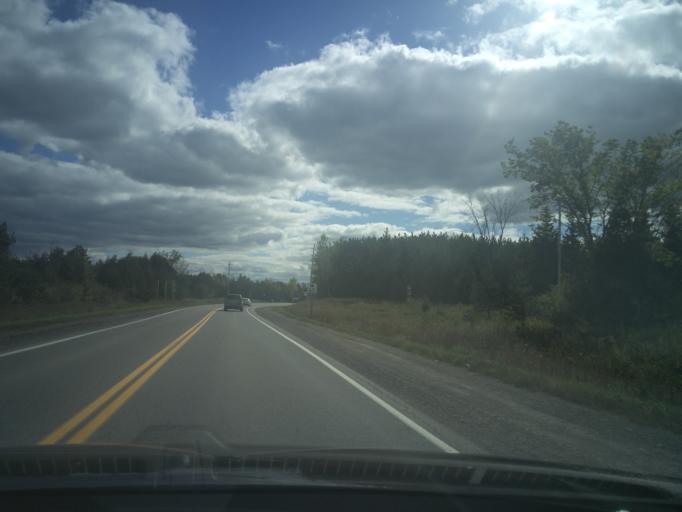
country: CA
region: Ontario
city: Carleton Place
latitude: 45.1077
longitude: -75.9726
